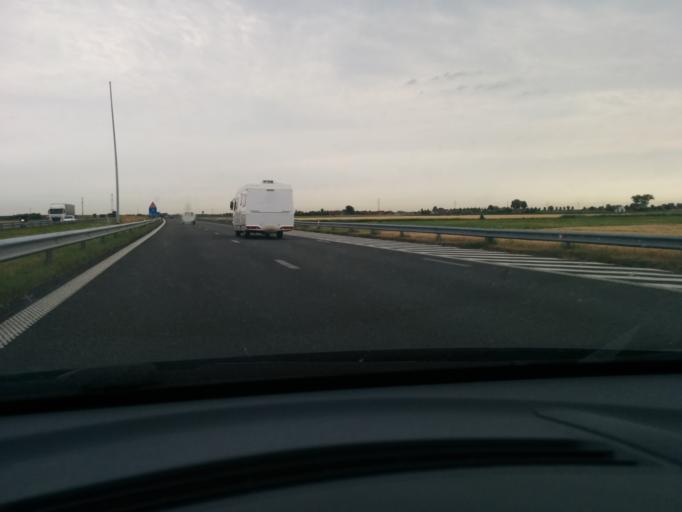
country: BE
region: Flanders
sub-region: Provincie West-Vlaanderen
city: Veurne
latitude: 51.0842
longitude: 2.7203
